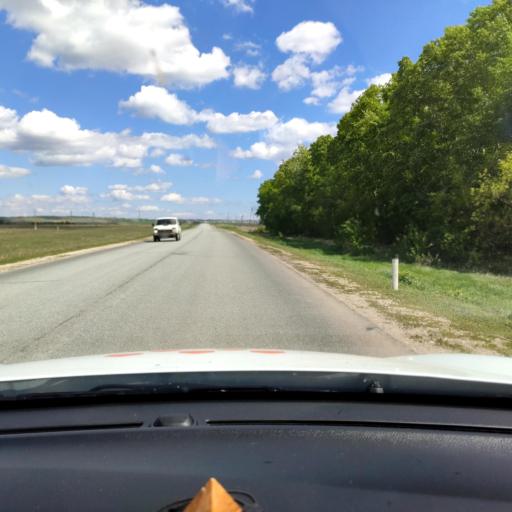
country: RU
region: Tatarstan
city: Kuybyshevskiy Zaton
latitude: 55.1618
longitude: 49.1972
